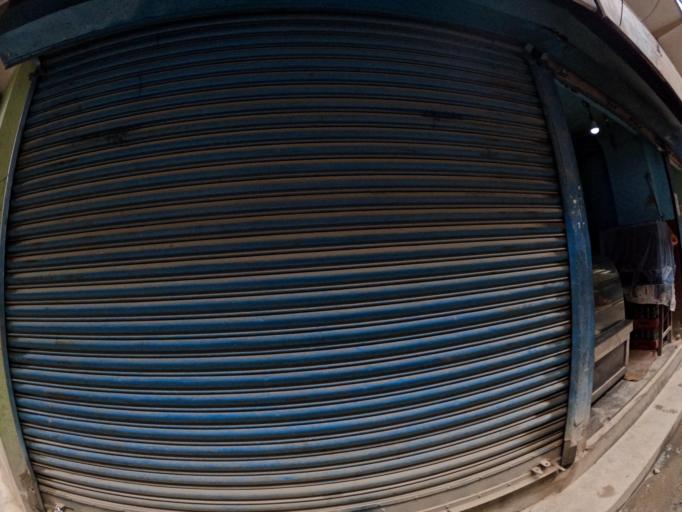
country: NP
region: Central Region
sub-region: Bagmati Zone
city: Kathmandu
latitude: 27.7362
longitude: 85.3108
